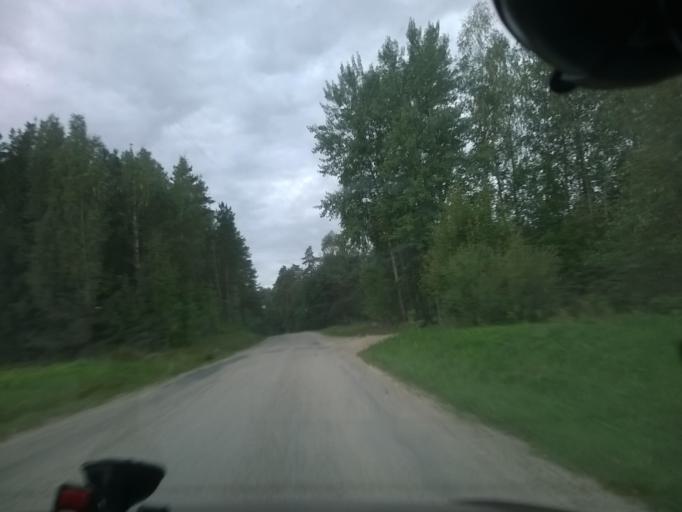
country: EE
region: Vorumaa
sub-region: Voru linn
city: Voru
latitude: 57.8183
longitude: 27.1178
